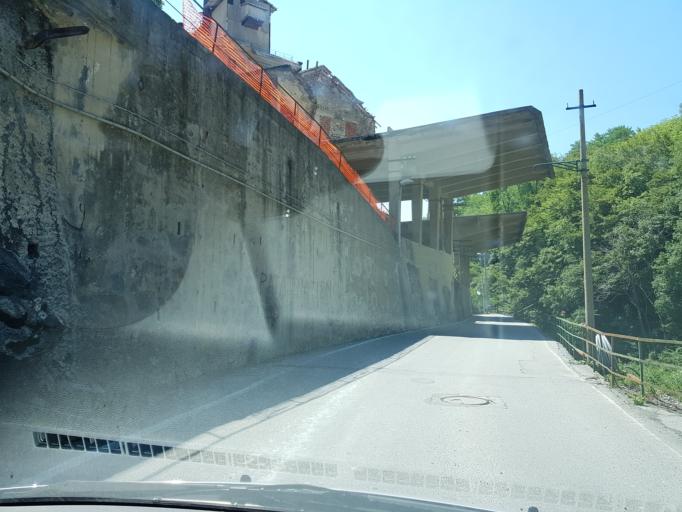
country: IT
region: Liguria
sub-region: Provincia di Genova
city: San Teodoro
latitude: 44.4431
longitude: 8.8549
